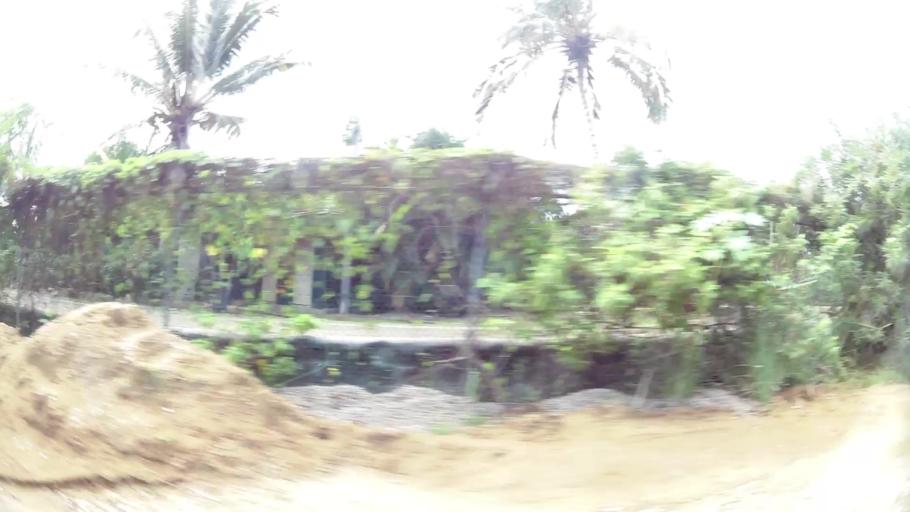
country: AG
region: Saint John
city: Saint John's
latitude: 17.1224
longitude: -61.8906
